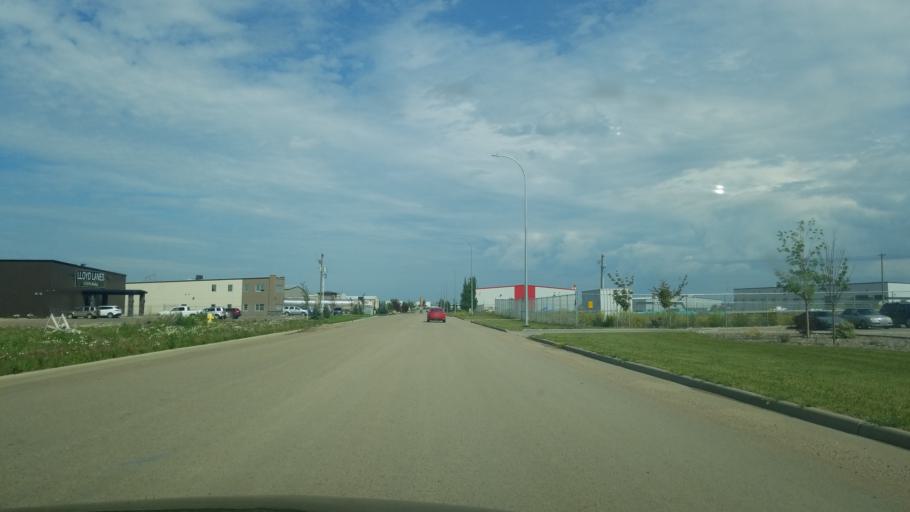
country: CA
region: Saskatchewan
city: Lloydminster
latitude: 53.2915
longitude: -110.0464
